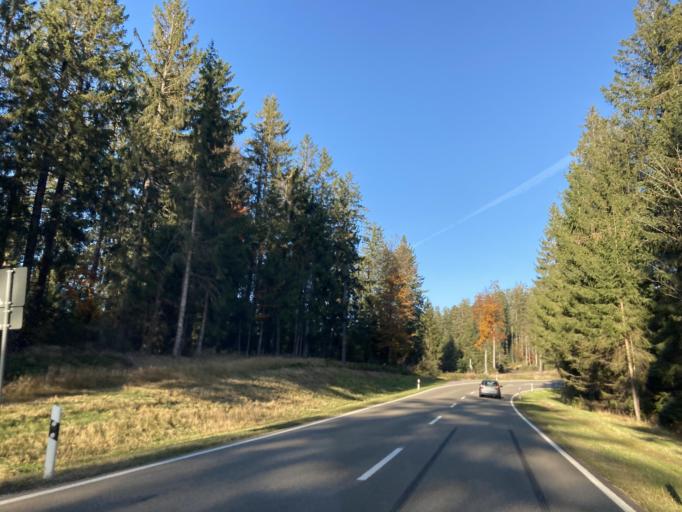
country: DE
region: Baden-Wuerttemberg
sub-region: Freiburg Region
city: Gutenbach
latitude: 47.9924
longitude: 8.1671
